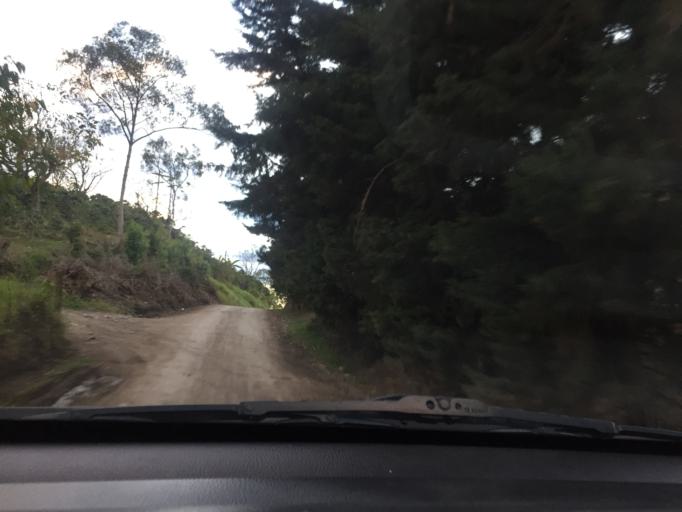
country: CO
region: Cundinamarca
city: Zipacon
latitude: 4.7018
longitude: -74.4092
